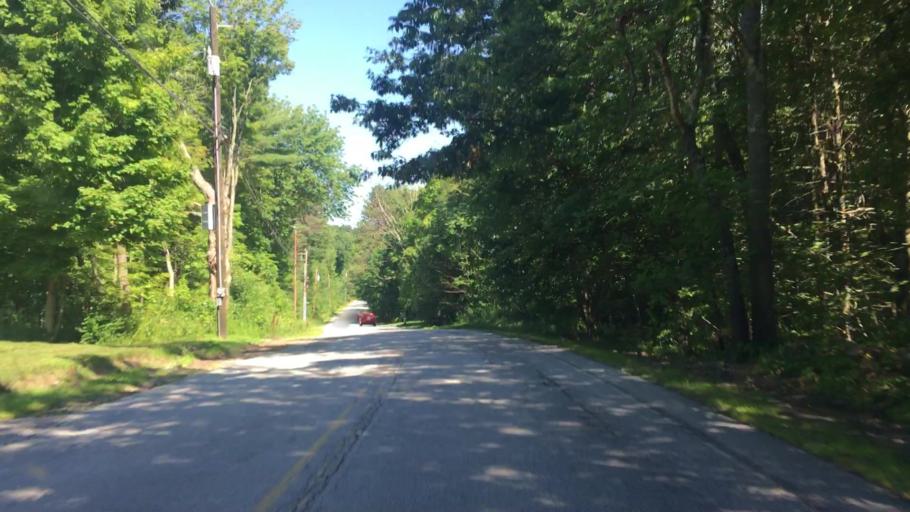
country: US
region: New Hampshire
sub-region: Merrimack County
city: South Hooksett
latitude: 43.0333
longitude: -71.3893
